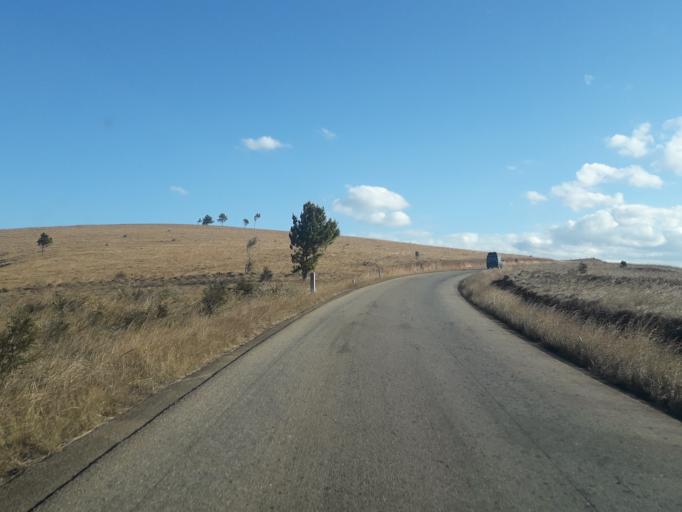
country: MG
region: Analamanga
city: Ankazobe
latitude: -17.9351
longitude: 47.1098
